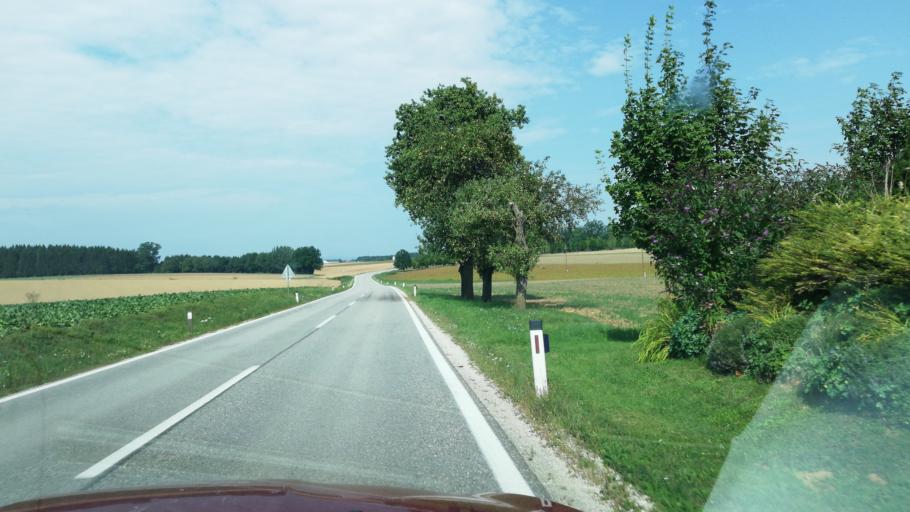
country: AT
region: Upper Austria
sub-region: Politischer Bezirk Steyr-Land
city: Sierning
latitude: 48.0599
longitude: 14.3158
